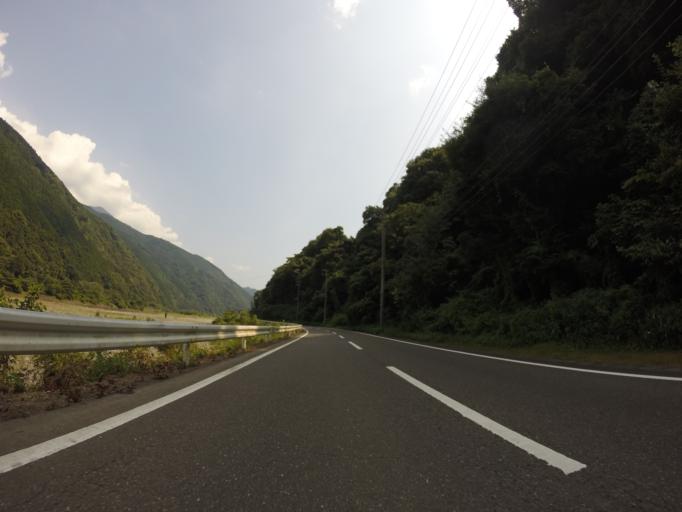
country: JP
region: Shizuoka
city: Shizuoka-shi
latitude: 35.1732
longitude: 138.3595
